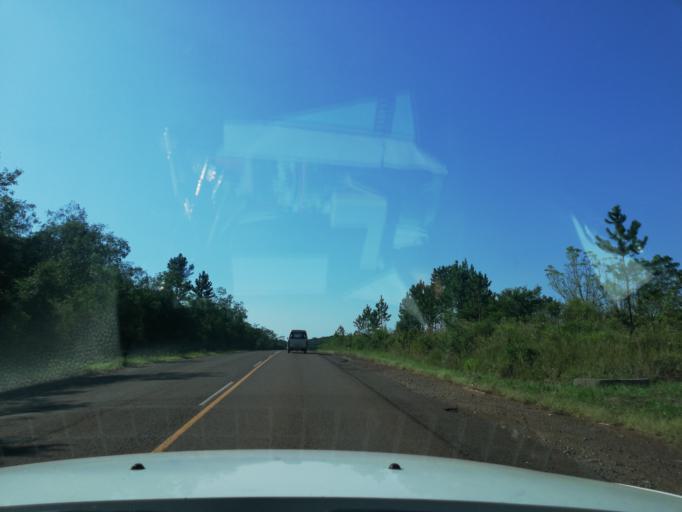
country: AR
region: Misiones
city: Almafuerte
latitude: -27.5476
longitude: -55.4289
